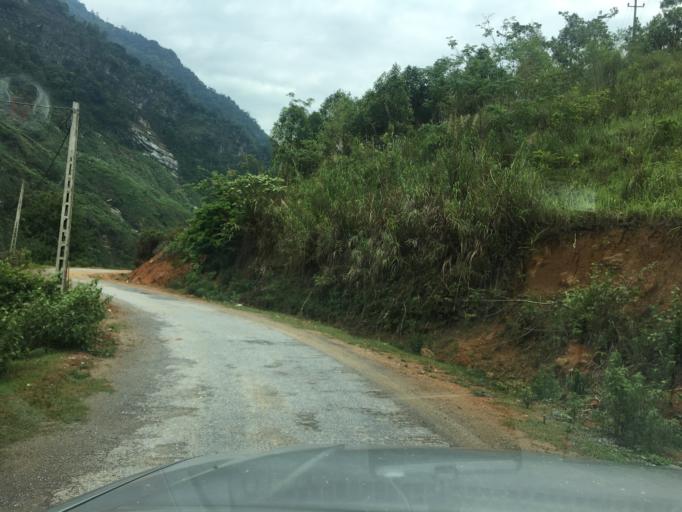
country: VN
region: Yen Bai
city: Son Thinh
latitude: 21.6808
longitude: 104.5582
